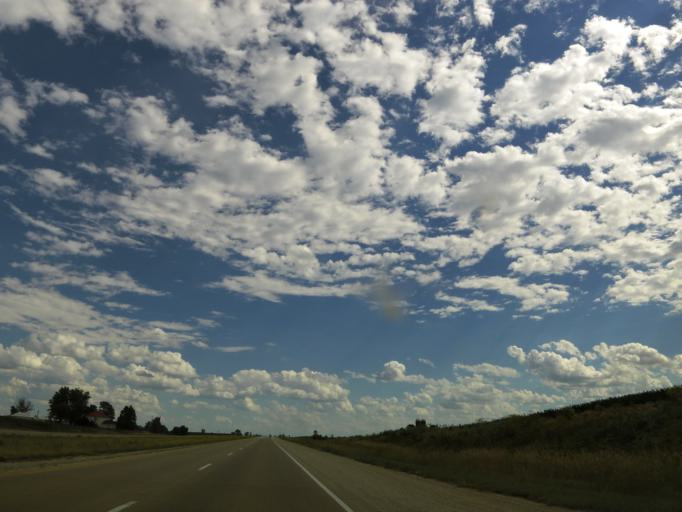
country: US
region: Iowa
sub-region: Henry County
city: Mount Pleasant
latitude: 40.8032
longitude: -91.5646
